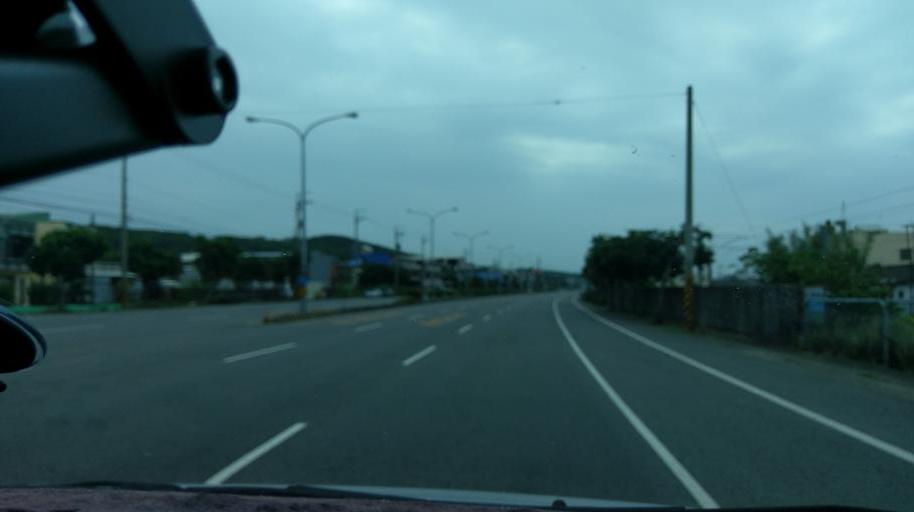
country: TW
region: Taiwan
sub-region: Miaoli
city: Miaoli
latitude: 24.5169
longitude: 120.6916
